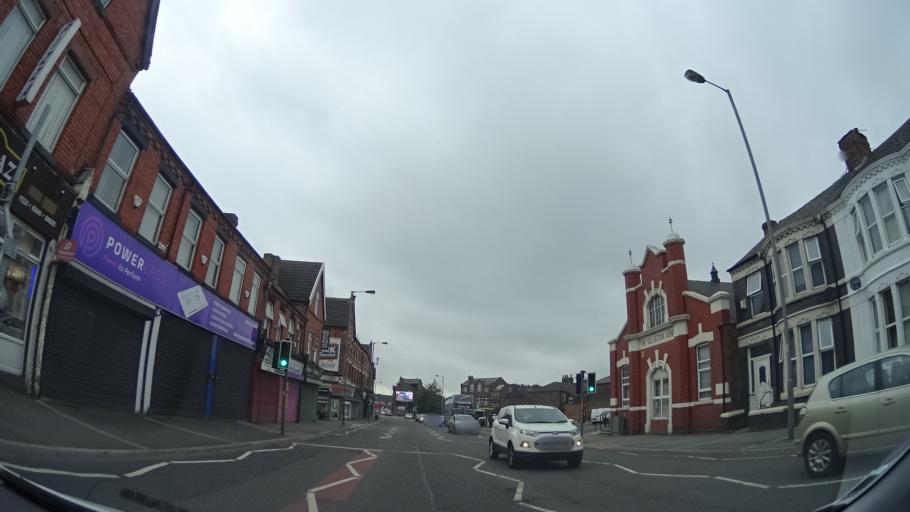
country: GB
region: England
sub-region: Liverpool
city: Liverpool
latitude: 53.4146
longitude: -2.9169
